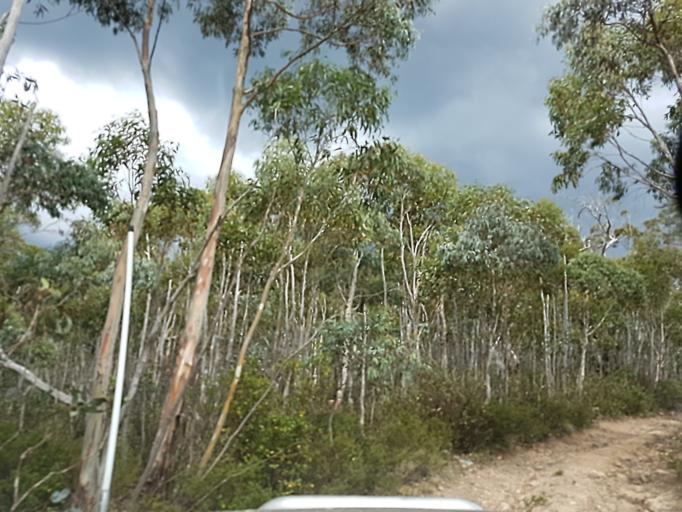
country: AU
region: New South Wales
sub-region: Snowy River
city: Jindabyne
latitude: -36.8771
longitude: 148.1792
